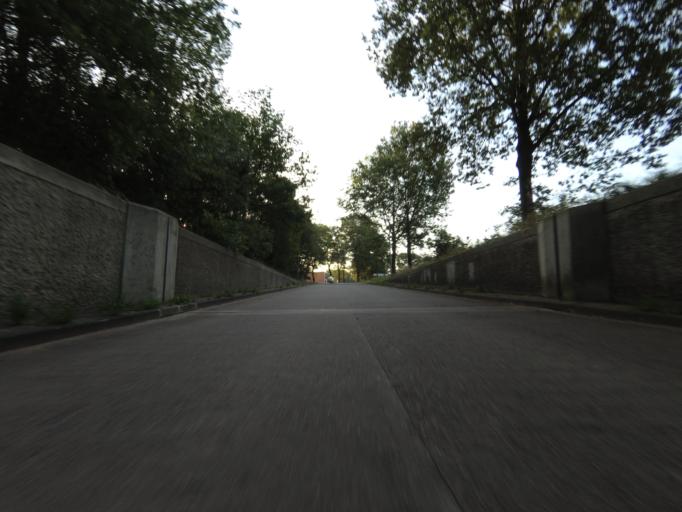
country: NL
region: Gelderland
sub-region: Gemeente Lochem
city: Laren
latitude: 52.2861
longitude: 6.3986
